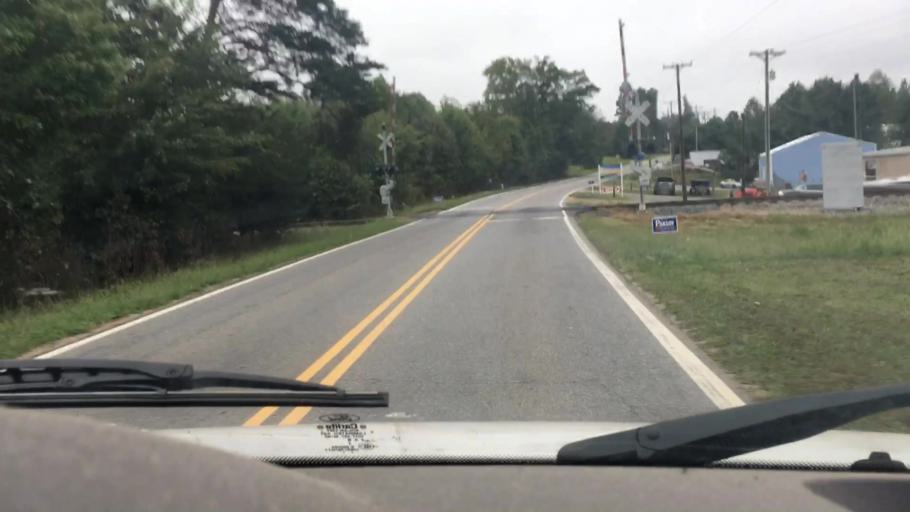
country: US
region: North Carolina
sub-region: Lincoln County
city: Denver
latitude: 35.5412
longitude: -81.0126
